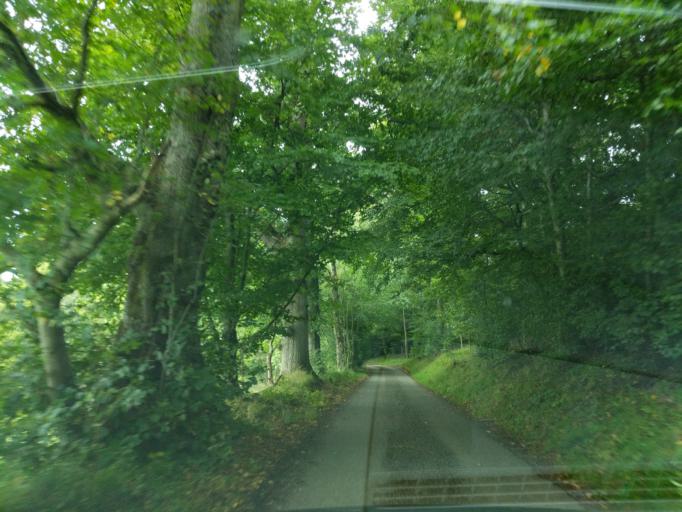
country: GB
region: Scotland
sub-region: The Scottish Borders
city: Galashiels
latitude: 55.5982
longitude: -2.7789
